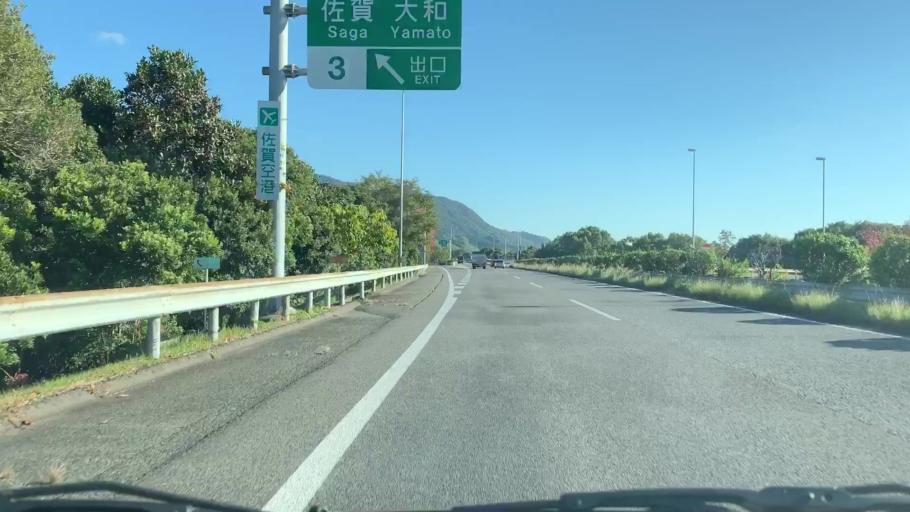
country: JP
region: Saga Prefecture
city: Saga-shi
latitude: 33.3210
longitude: 130.2763
